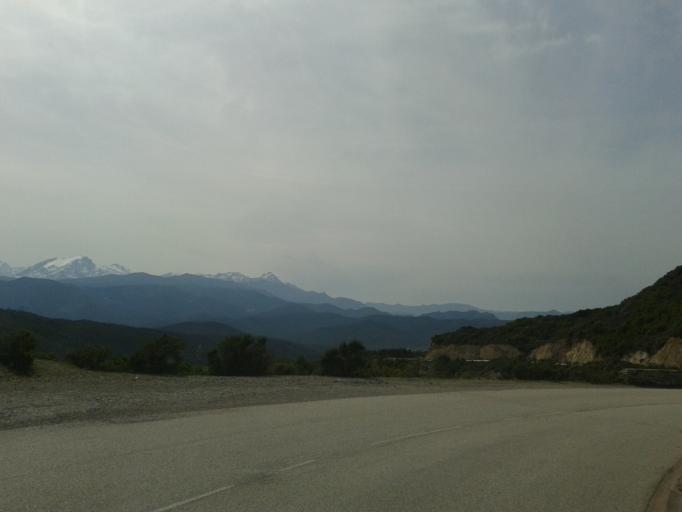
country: FR
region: Corsica
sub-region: Departement de la Haute-Corse
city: Saint-Florent
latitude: 42.6622
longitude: 9.1343
